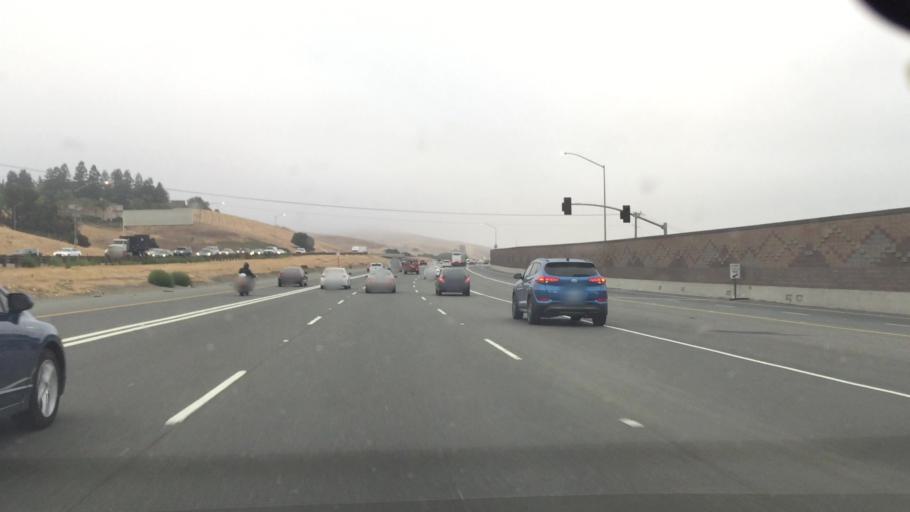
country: US
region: California
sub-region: Santa Clara County
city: Milpitas
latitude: 37.4931
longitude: -121.9208
